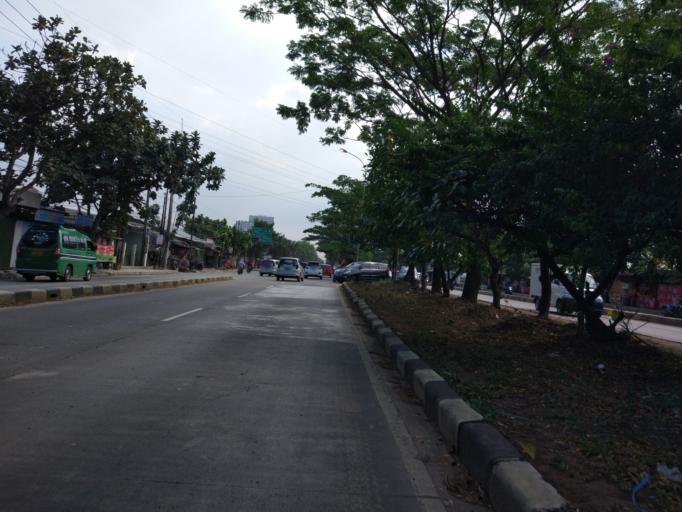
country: ID
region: West Java
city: Cileunyi
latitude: -6.9360
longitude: 107.7076
